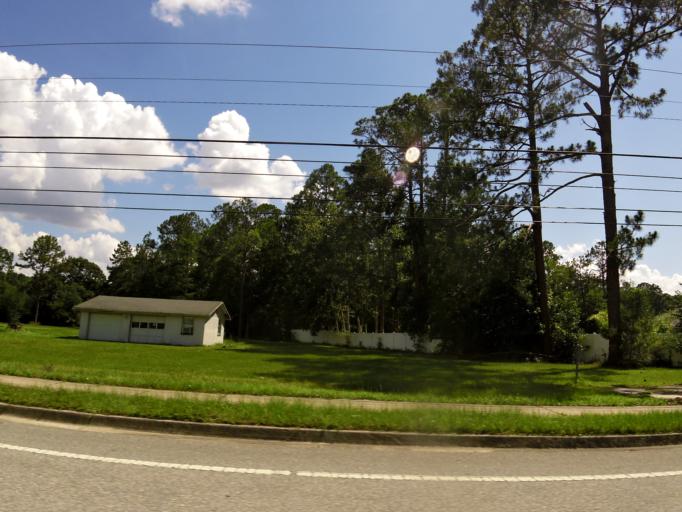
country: US
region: Florida
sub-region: Saint Johns County
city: Fruit Cove
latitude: 30.1500
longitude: -81.5796
